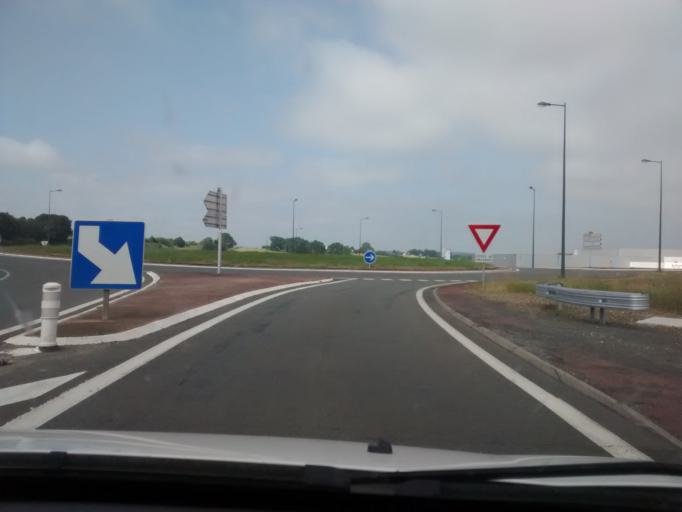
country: FR
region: Pays de la Loire
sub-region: Departement de la Sarthe
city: Cherre
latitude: 48.1495
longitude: 0.6857
